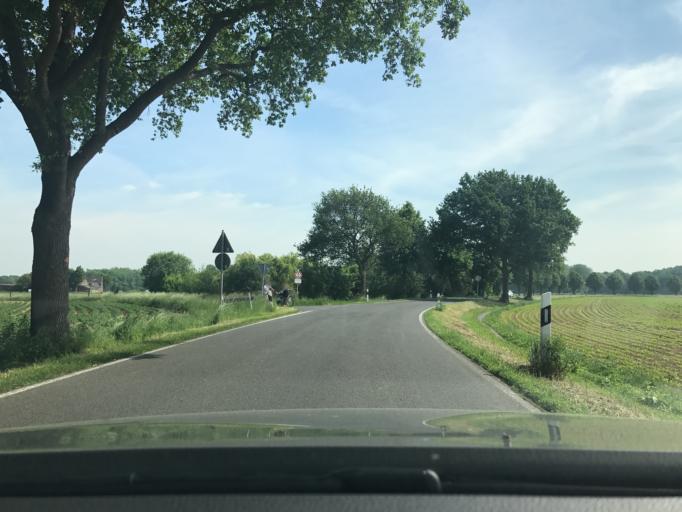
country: DE
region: North Rhine-Westphalia
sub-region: Regierungsbezirk Dusseldorf
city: Viersen
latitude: 51.3070
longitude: 6.3992
